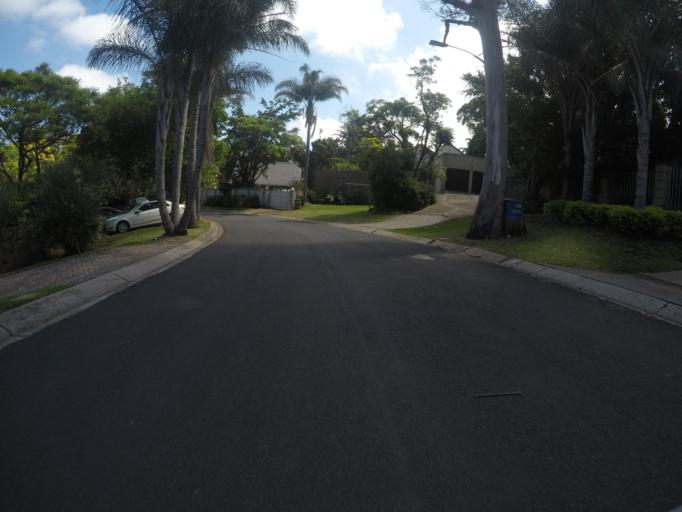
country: ZA
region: Eastern Cape
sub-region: Buffalo City Metropolitan Municipality
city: East London
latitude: -32.9762
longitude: 27.9057
